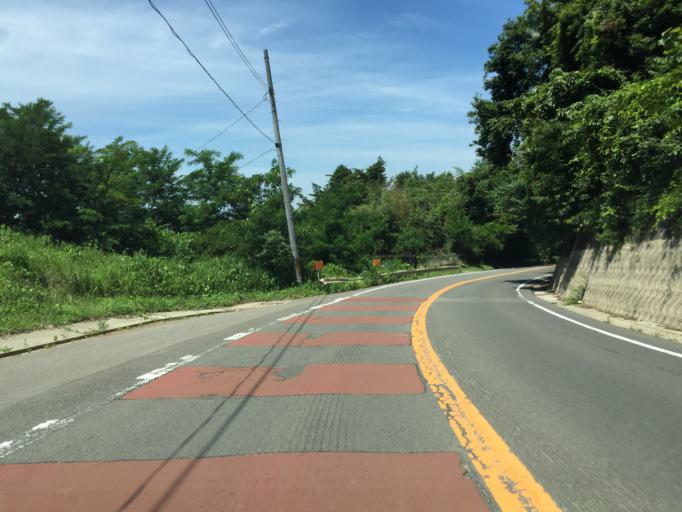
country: JP
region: Fukushima
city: Fukushima-shi
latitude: 37.7521
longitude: 140.5216
